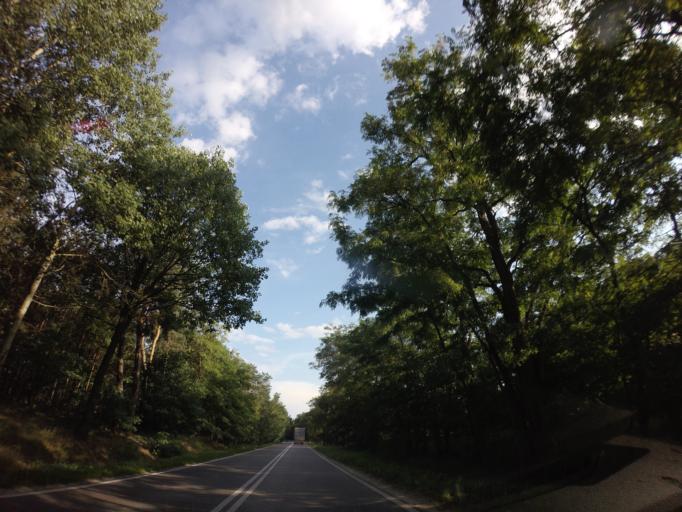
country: PL
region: Lublin Voivodeship
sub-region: Powiat lubartowski
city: Jeziorzany
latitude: 51.5815
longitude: 22.2820
